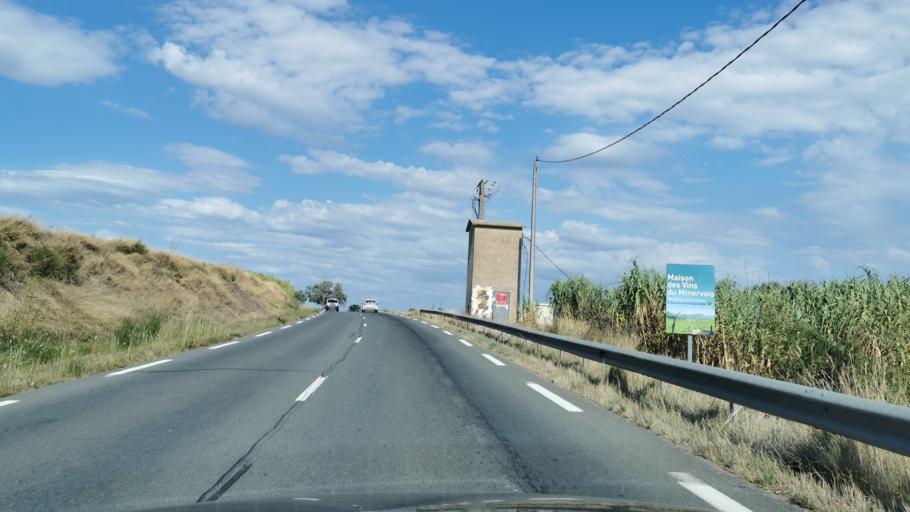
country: FR
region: Languedoc-Roussillon
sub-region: Departement de l'Herault
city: Olonzac
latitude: 43.2596
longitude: 2.7032
